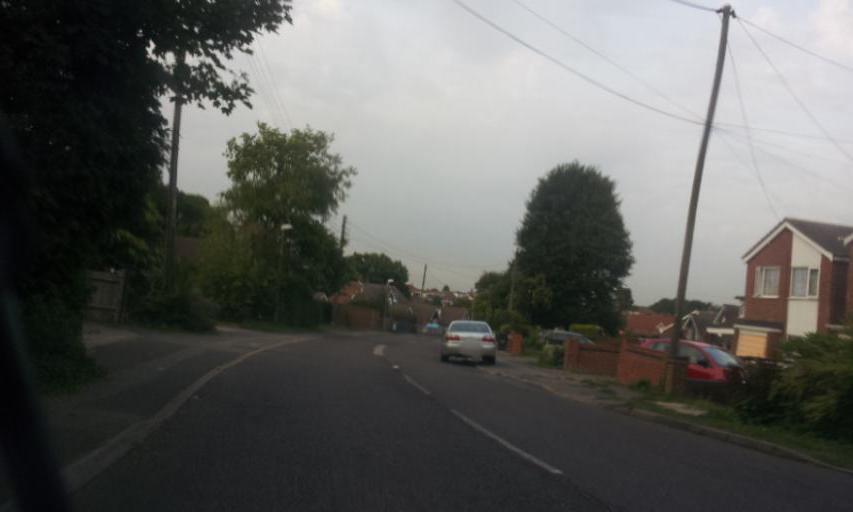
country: GB
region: England
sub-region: Kent
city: Boxley
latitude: 51.3350
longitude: 0.5168
